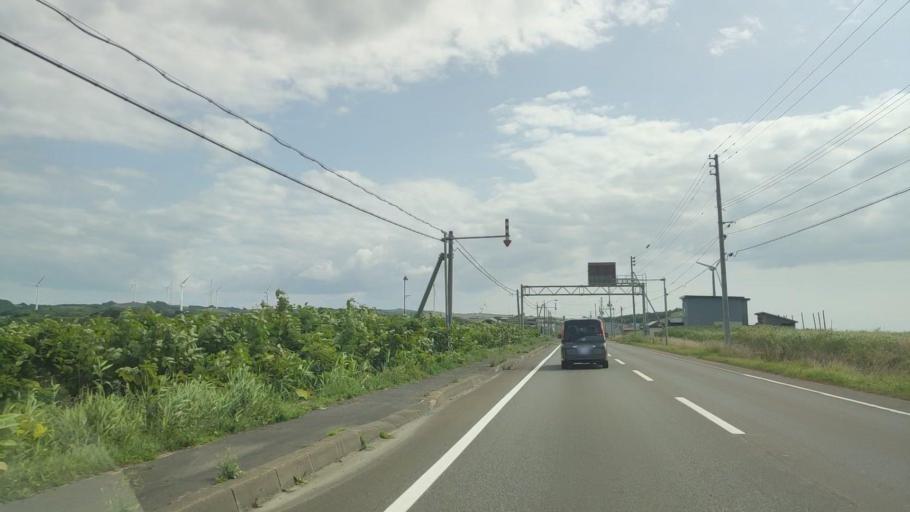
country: JP
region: Hokkaido
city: Rumoi
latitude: 44.2673
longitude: 141.6551
